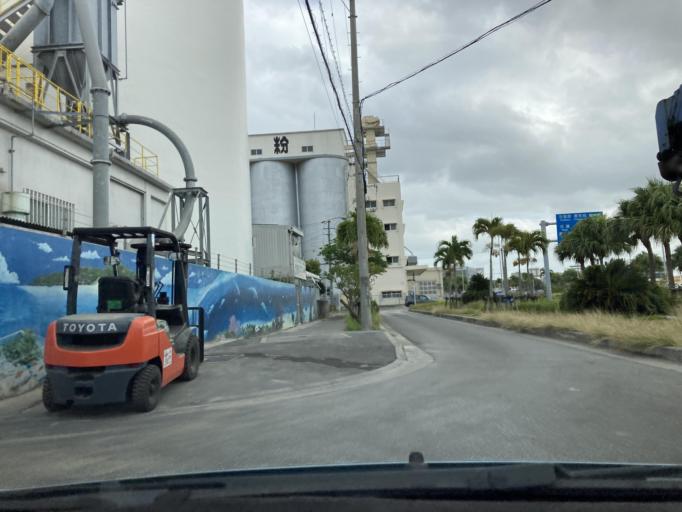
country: JP
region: Okinawa
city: Naha-shi
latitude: 26.2107
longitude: 127.6715
